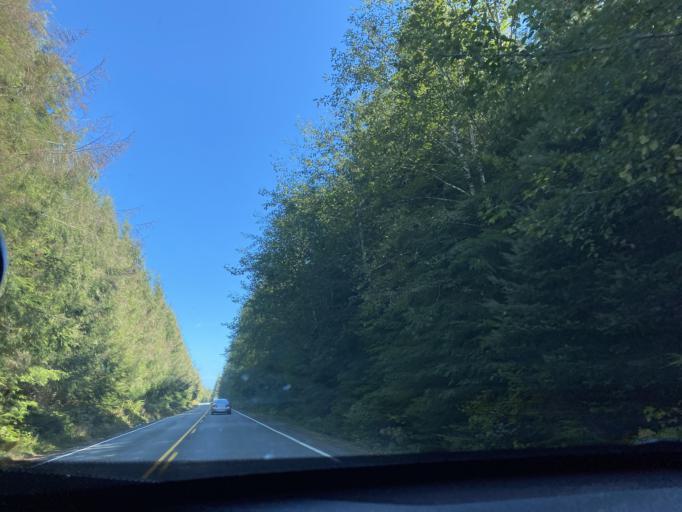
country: US
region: Washington
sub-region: Clallam County
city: Forks
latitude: 47.9179
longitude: -124.5235
